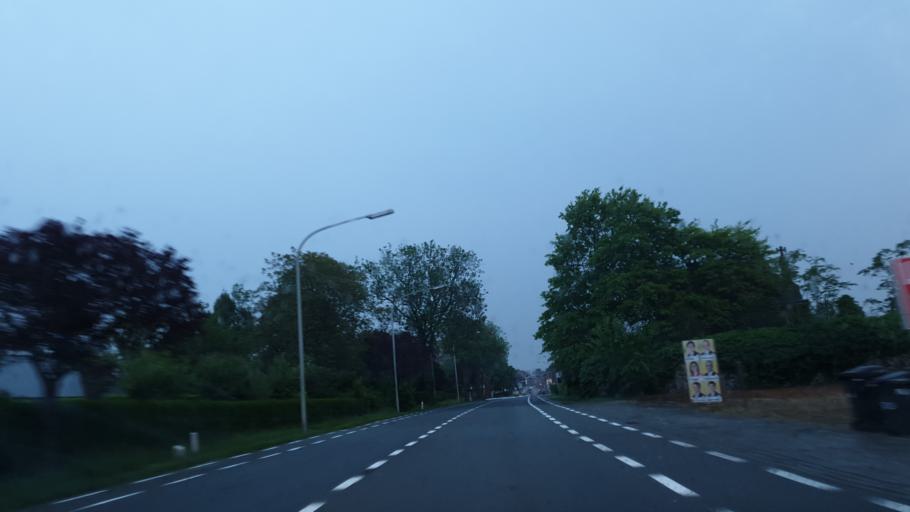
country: BE
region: Flanders
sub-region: Provincie West-Vlaanderen
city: Ieper
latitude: 50.8590
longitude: 2.8696
